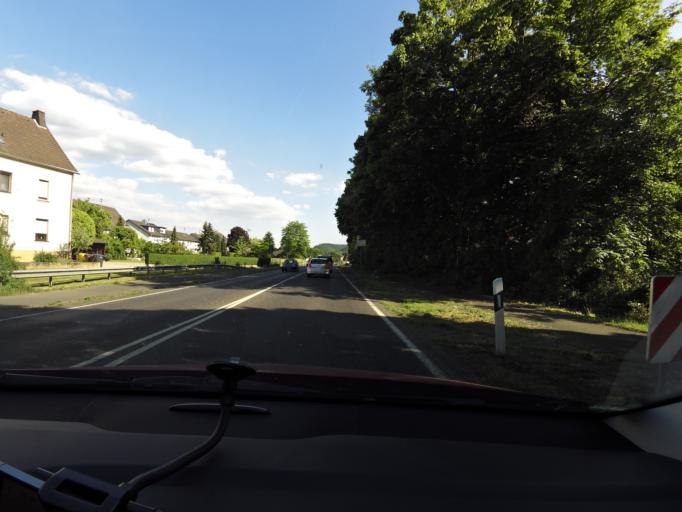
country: DE
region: Rheinland-Pfalz
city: Bad Breisig
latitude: 50.5180
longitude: 7.2905
